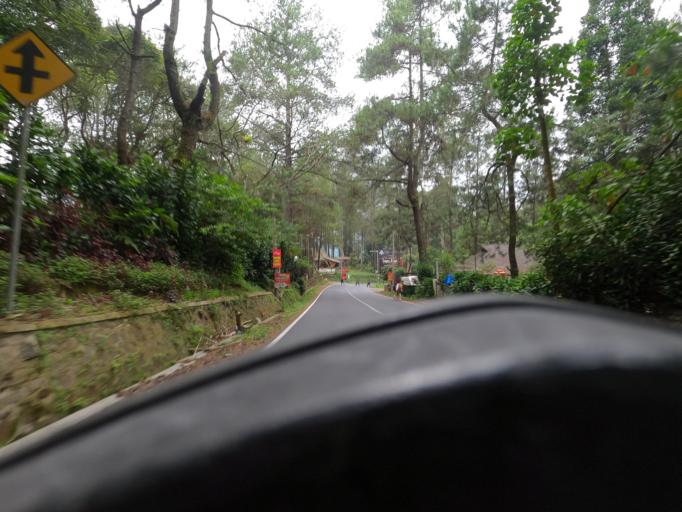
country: ID
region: West Java
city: Lembang
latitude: -6.7824
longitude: 107.6495
